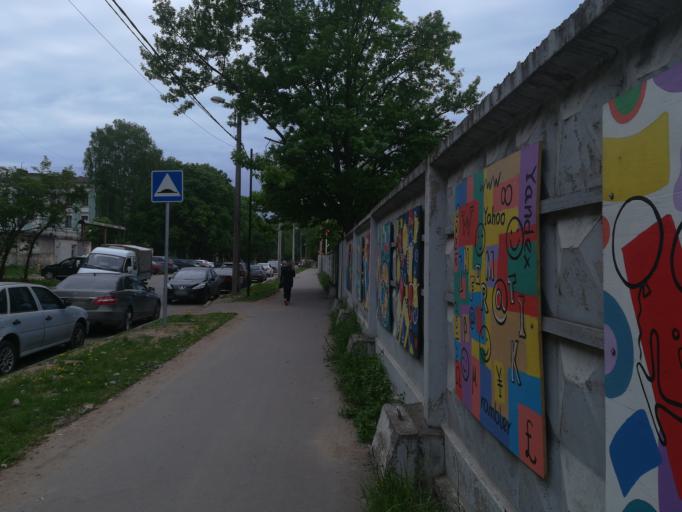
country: RU
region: St.-Petersburg
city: Vasyl'evsky Ostrov
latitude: 59.9517
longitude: 30.2604
